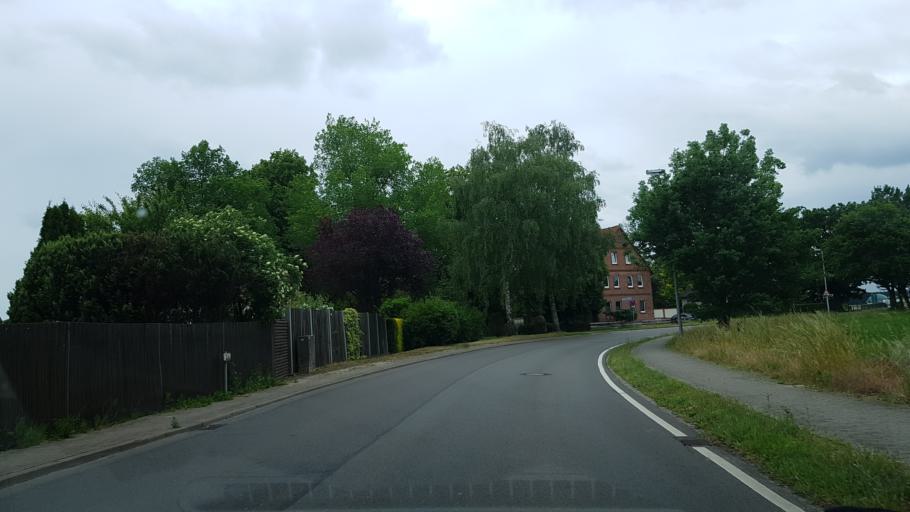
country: DE
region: Lower Saxony
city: Celle
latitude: 52.6516
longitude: 10.0583
